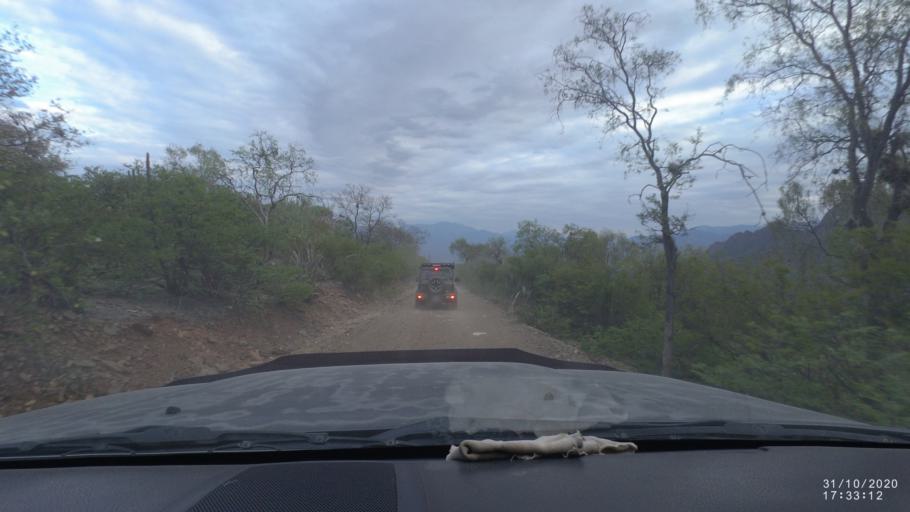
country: BO
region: Chuquisaca
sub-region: Provincia Zudanez
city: Mojocoya
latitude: -18.5994
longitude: -64.5508
